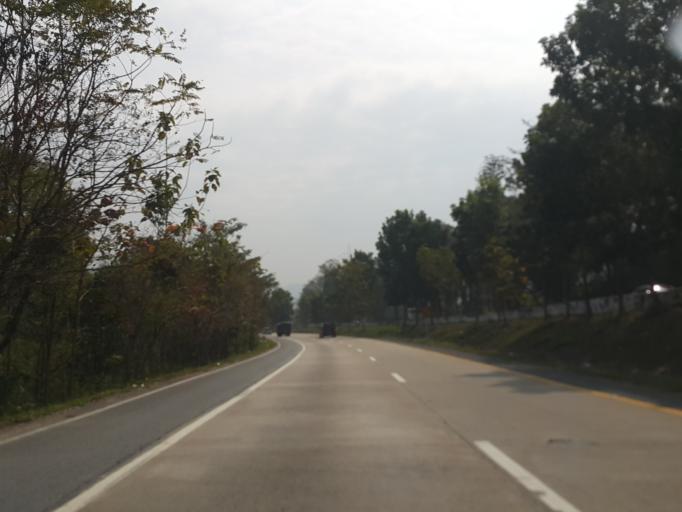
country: TH
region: Lamphun
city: Mae Tha
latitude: 18.4611
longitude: 99.1796
